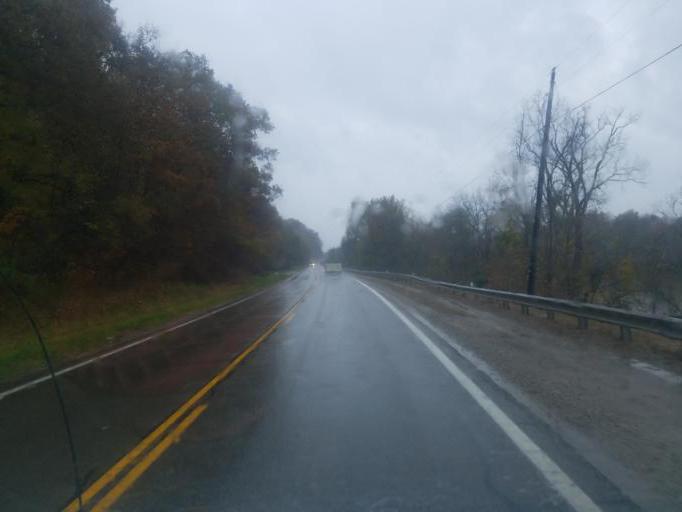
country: US
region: Ohio
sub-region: Muskingum County
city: Pleasant Grove
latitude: 39.8625
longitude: -81.8997
